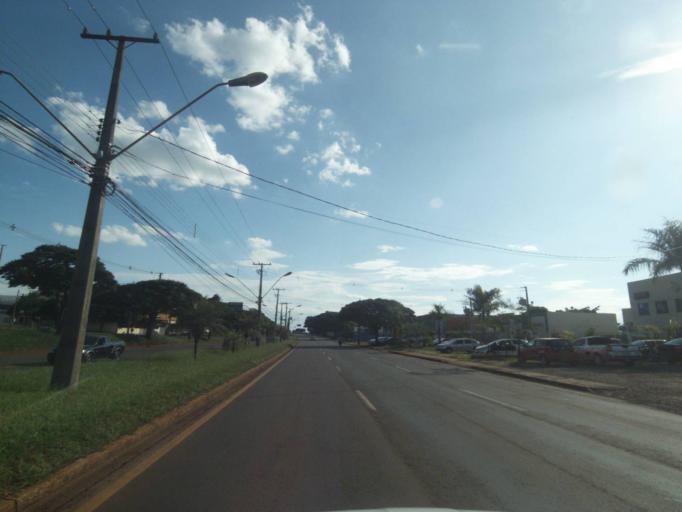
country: BR
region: Parana
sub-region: Londrina
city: Londrina
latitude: -23.3543
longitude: -51.1490
